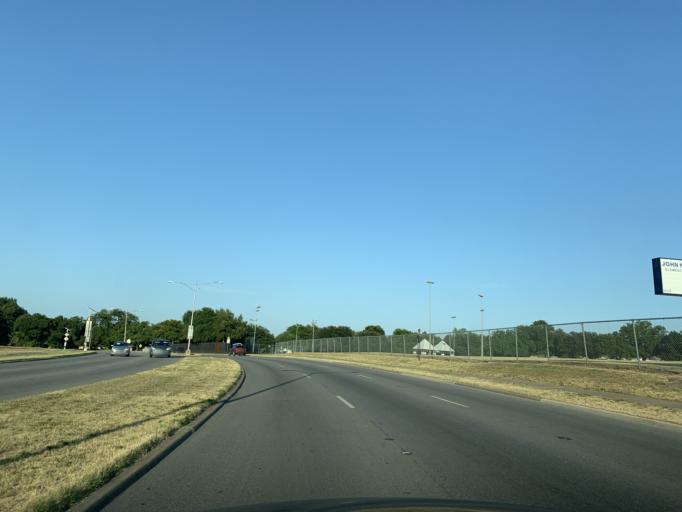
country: US
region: Texas
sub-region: Dallas County
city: Dallas
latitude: 32.7125
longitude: -96.7954
